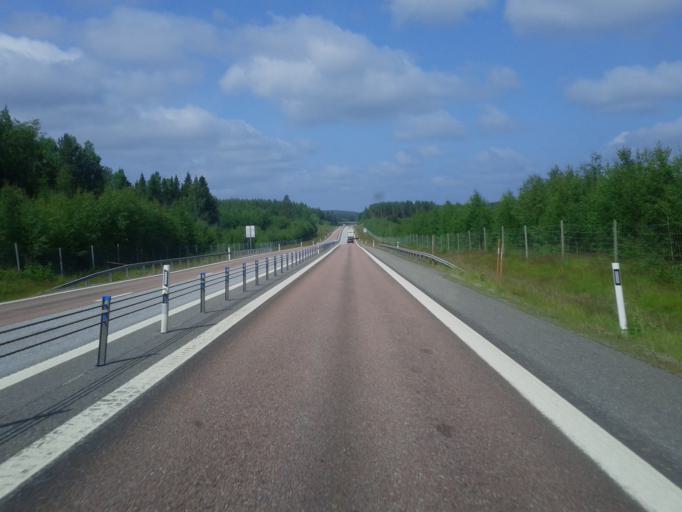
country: SE
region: Vaesterbotten
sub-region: Skelleftea Kommun
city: Soedra Bergsbyn
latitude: 64.6915
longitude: 21.0354
